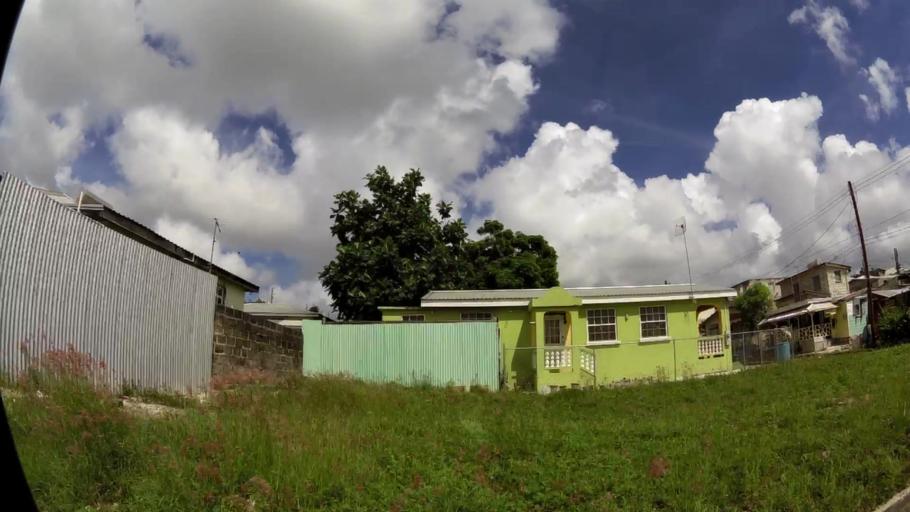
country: BB
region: Saint Michael
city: Bridgetown
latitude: 13.1252
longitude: -59.6170
